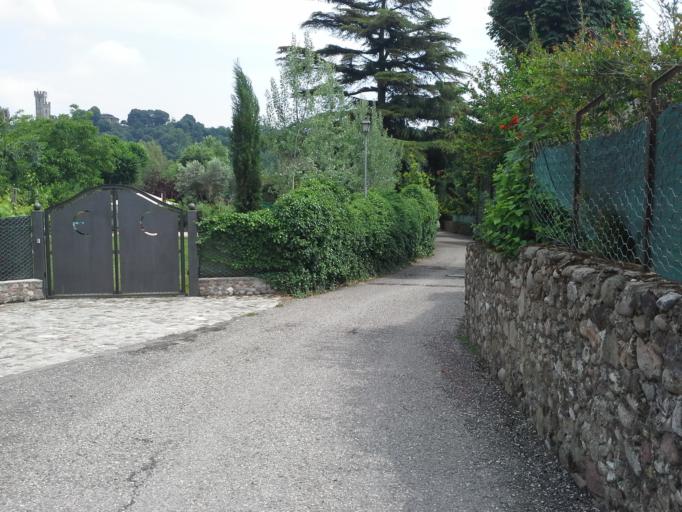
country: IT
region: Veneto
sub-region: Provincia di Verona
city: Valeggio sul Mincio
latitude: 45.3554
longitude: 10.7227
